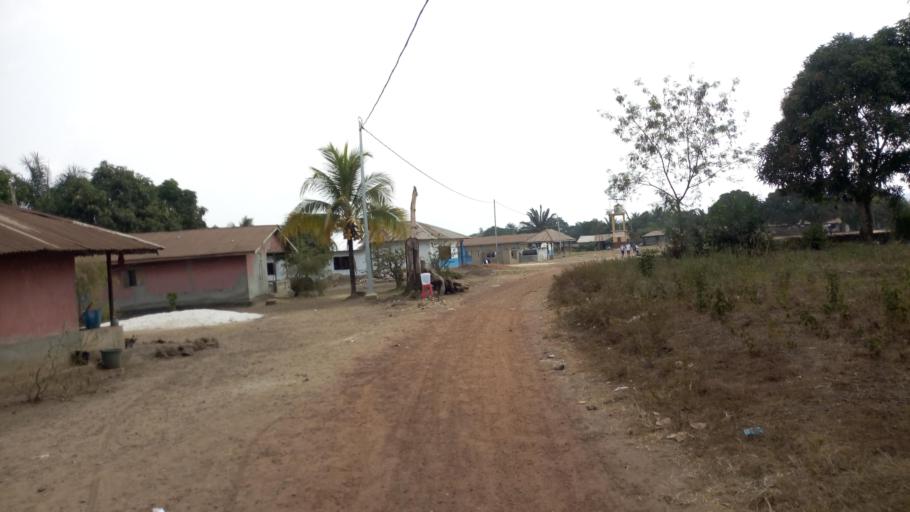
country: SL
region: Southern Province
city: Mogbwemo
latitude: 7.7882
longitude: -12.3035
